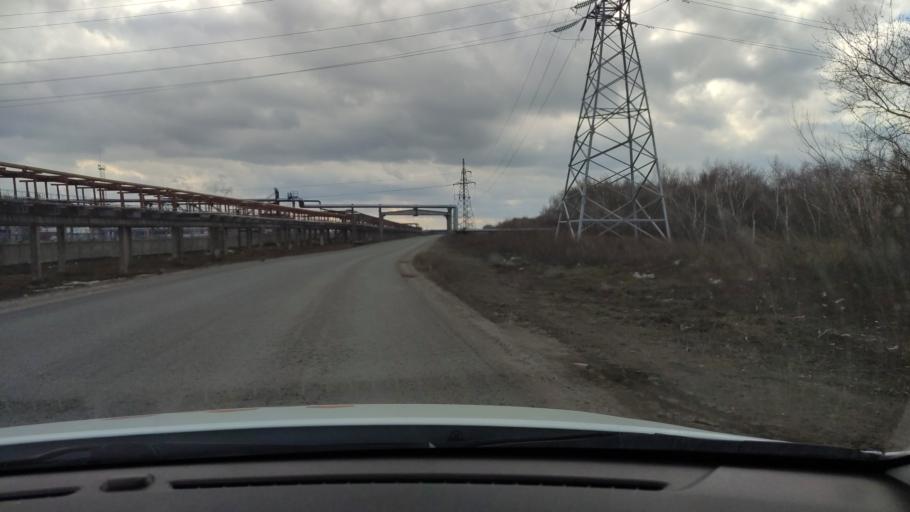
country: RU
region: Tatarstan
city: Staroye Arakchino
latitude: 55.8783
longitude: 48.9761
